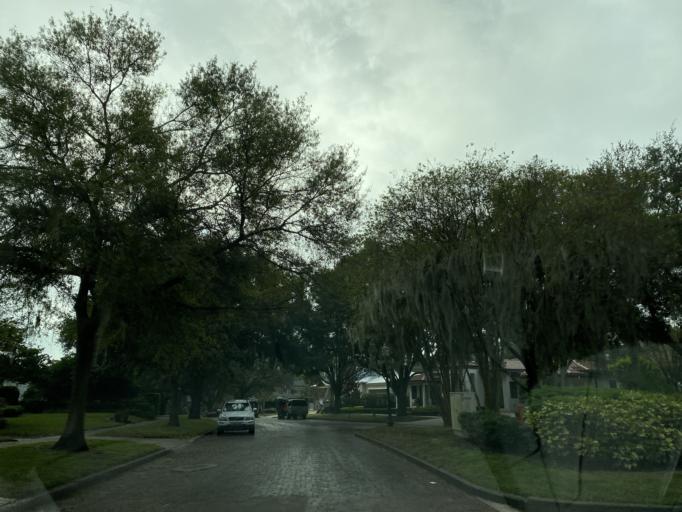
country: US
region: Florida
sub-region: Orange County
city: Orlando
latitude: 28.5613
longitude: -81.3951
